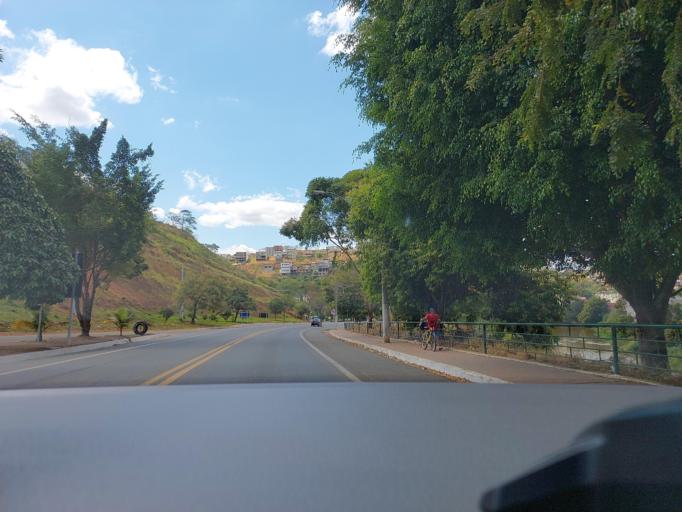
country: BR
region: Minas Gerais
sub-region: Muriae
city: Muriae
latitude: -21.1271
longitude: -42.3572
